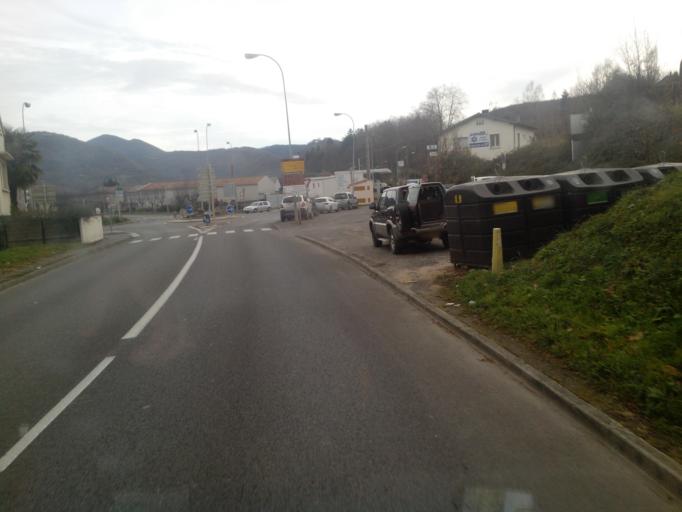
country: FR
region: Midi-Pyrenees
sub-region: Departement de l'Ariege
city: Saint-Girons
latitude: 42.9807
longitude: 1.1433
